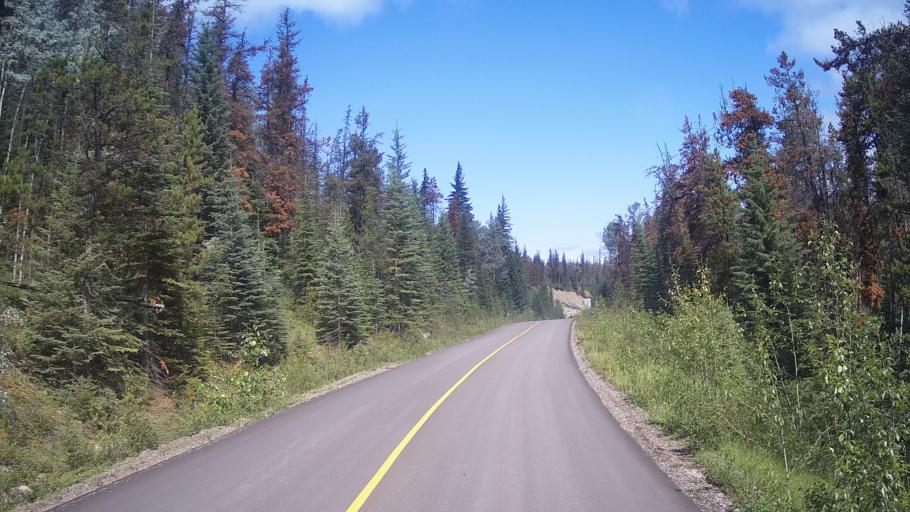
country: CA
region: Alberta
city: Jasper Park Lodge
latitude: 52.6639
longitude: -117.8878
